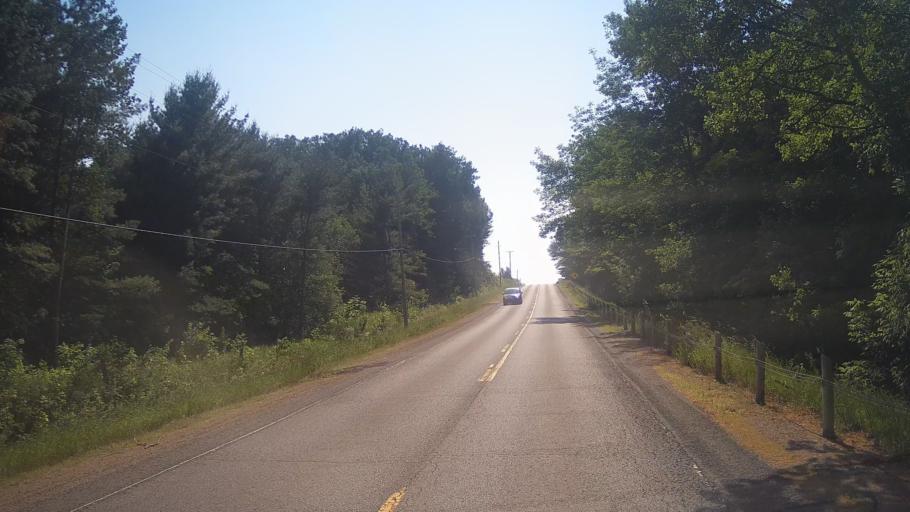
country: CA
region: Ontario
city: Pembroke
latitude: 45.6066
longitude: -77.2173
